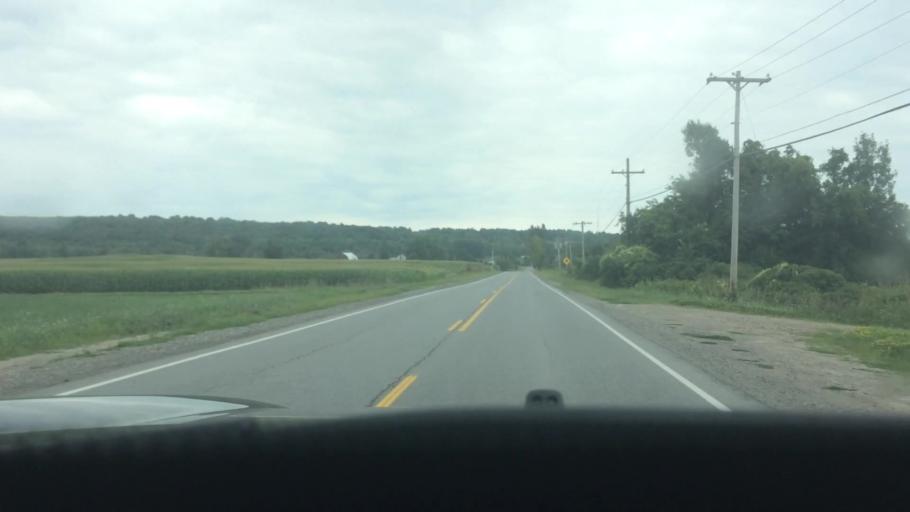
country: US
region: New York
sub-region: St. Lawrence County
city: Canton
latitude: 44.5522
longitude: -75.1084
